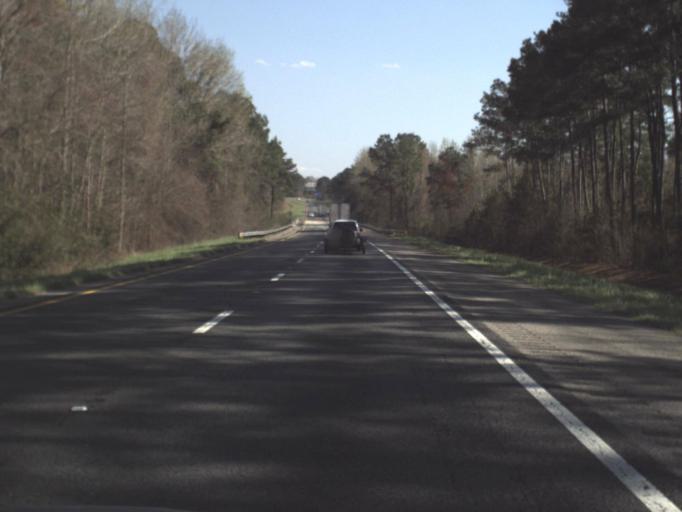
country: US
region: Florida
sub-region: Gadsden County
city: Gretna
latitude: 30.5858
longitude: -84.7154
